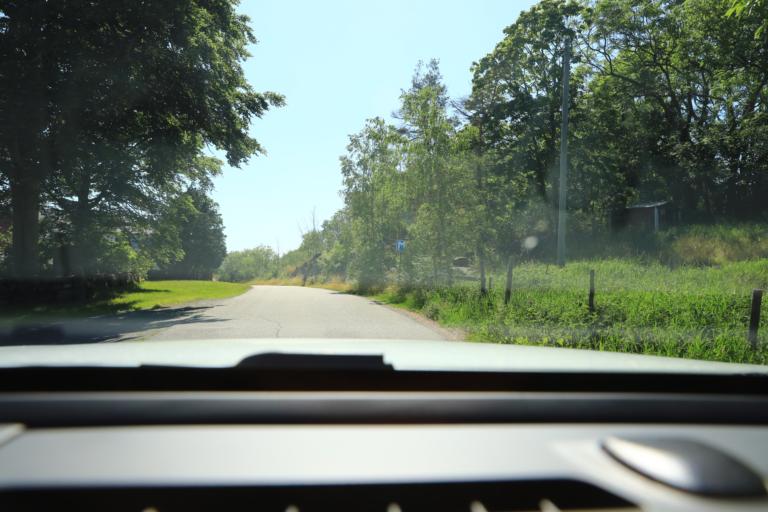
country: SE
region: Halland
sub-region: Varbergs Kommun
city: Veddige
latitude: 57.1888
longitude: 12.3205
